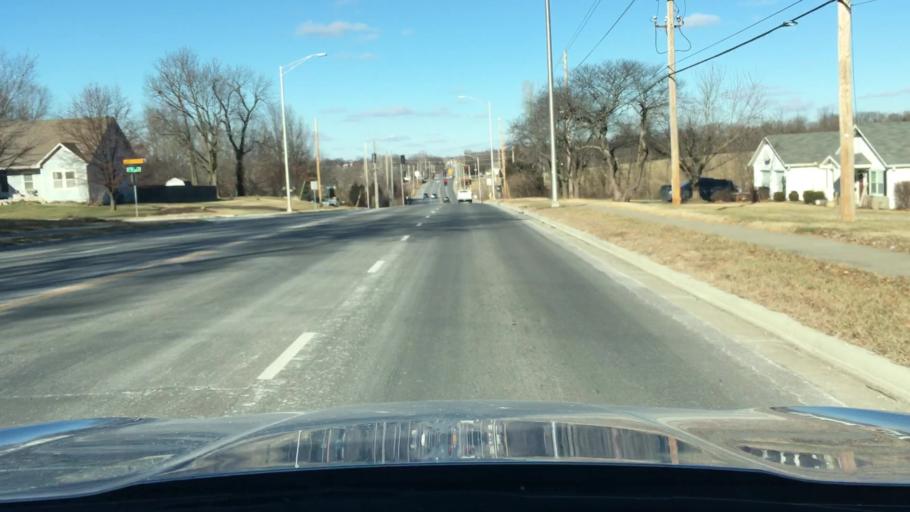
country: US
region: Missouri
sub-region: Jackson County
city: Lees Summit
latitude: 38.8956
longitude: -94.3960
